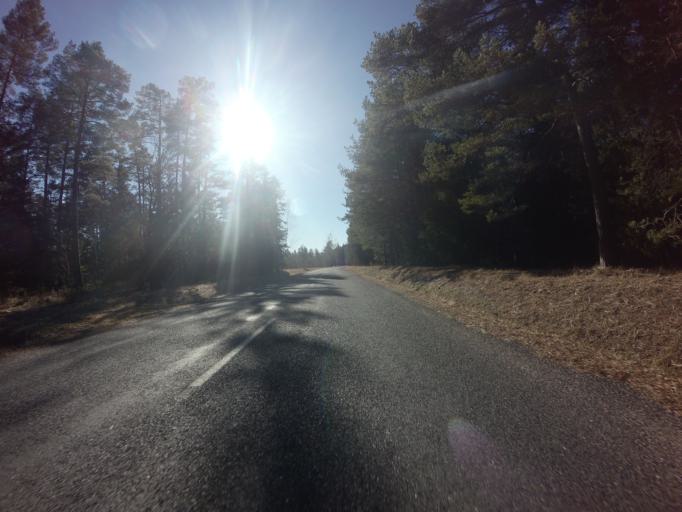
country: EE
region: Saare
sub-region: Kuressaare linn
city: Kuressaare
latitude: 58.5845
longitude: 22.5637
